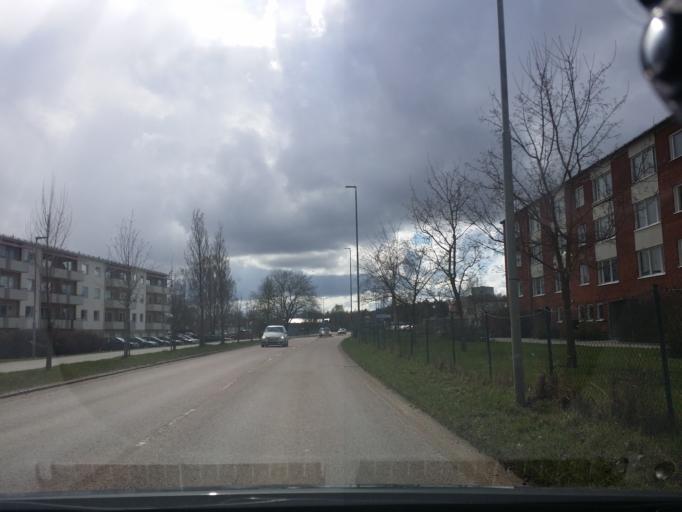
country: SE
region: Vaestmanland
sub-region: Sala Kommun
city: Sala
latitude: 59.9239
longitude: 16.5894
